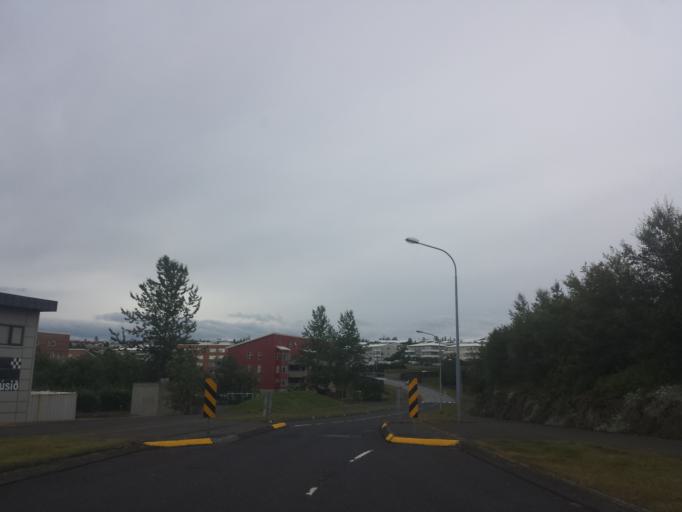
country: IS
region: Capital Region
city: Kopavogur
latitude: 64.0969
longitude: -21.8721
